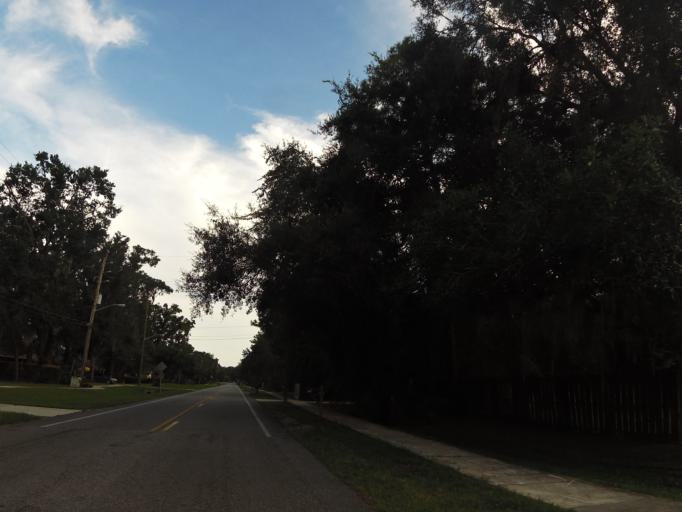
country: US
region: Florida
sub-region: Saint Johns County
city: Fruit Cove
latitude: 30.1073
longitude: -81.6355
